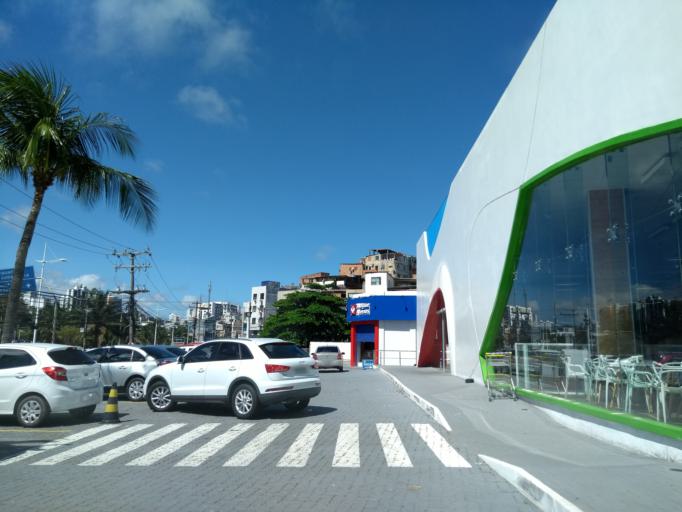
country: BR
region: Bahia
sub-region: Salvador
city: Salvador
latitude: -13.0058
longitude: -38.4845
